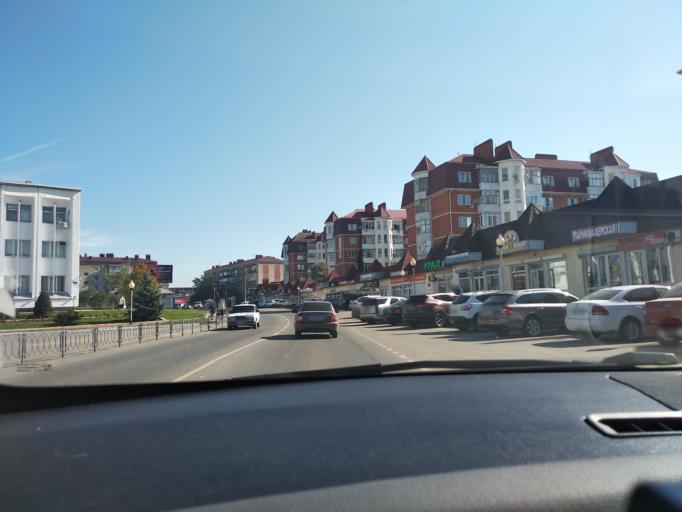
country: RU
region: Krasnodarskiy
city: Goryachiy Klyuch
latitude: 44.6338
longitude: 39.1368
